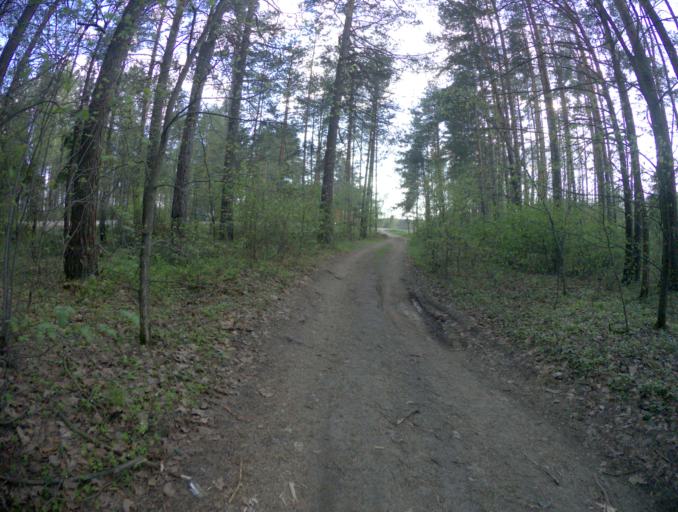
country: RU
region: Vladimir
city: Raduzhnyy
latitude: 56.0294
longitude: 40.4010
